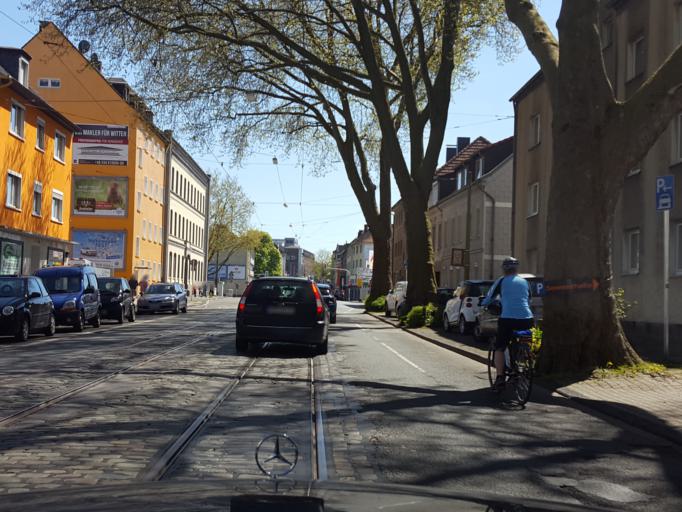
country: DE
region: North Rhine-Westphalia
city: Witten
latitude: 51.4477
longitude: 7.3306
